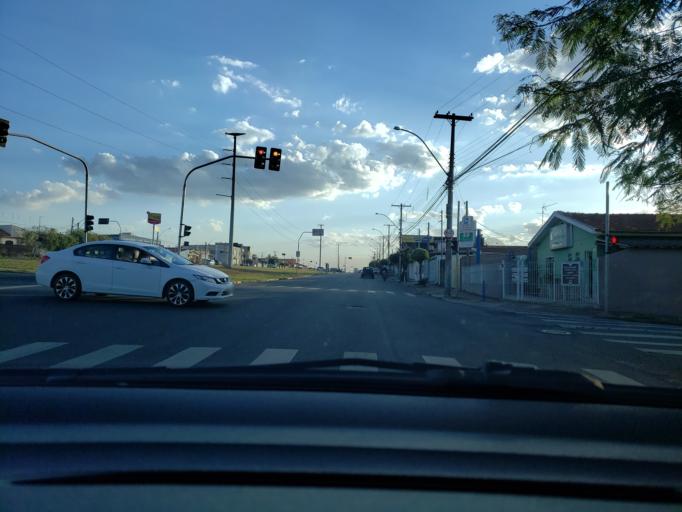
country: BR
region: Sao Paulo
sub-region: Americana
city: Americana
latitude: -22.7384
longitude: -47.3712
